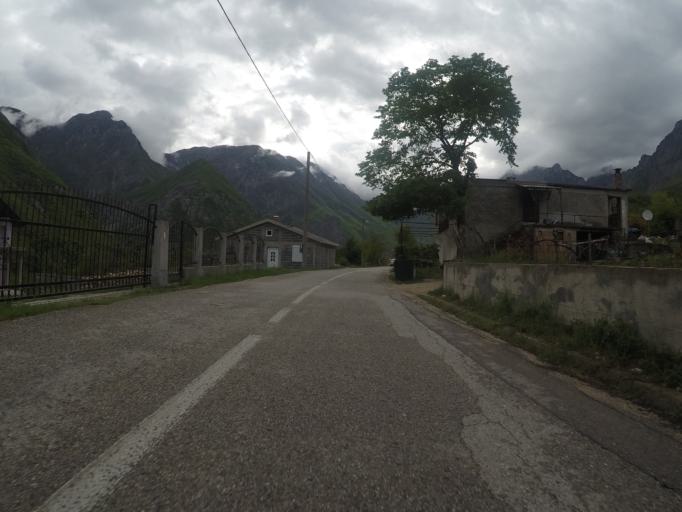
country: BA
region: Federation of Bosnia and Herzegovina
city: Siroki Brijeg
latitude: 43.5406
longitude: 17.5860
